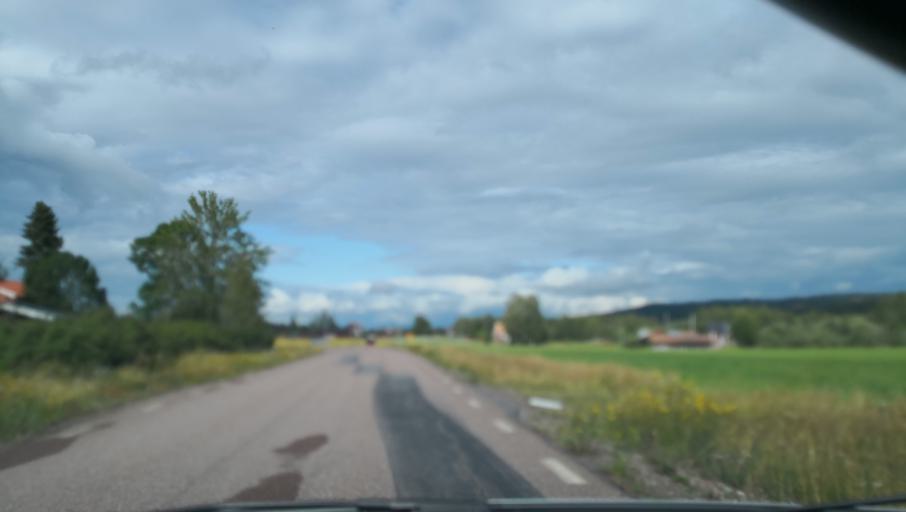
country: SE
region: Dalarna
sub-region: Borlange Kommun
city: Ornas
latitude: 60.4330
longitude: 15.6093
